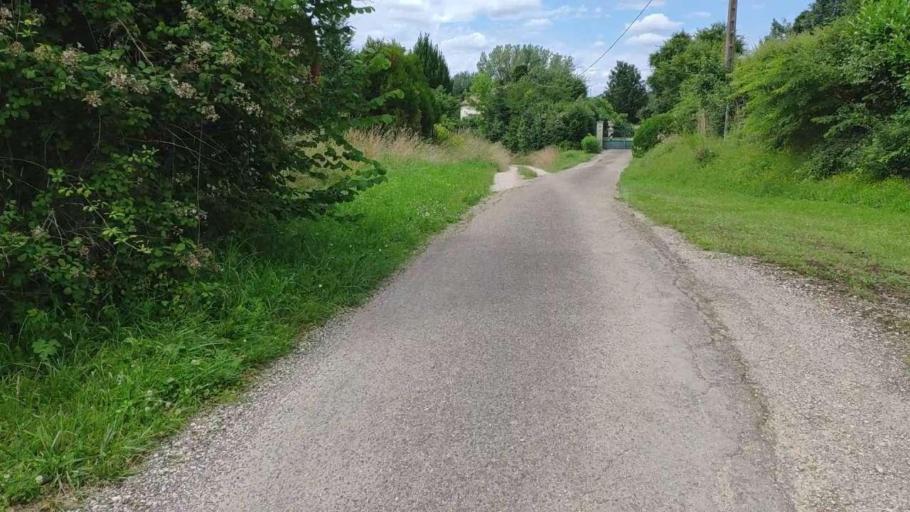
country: FR
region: Franche-Comte
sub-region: Departement du Jura
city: Chaussin
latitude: 46.8707
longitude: 5.4271
